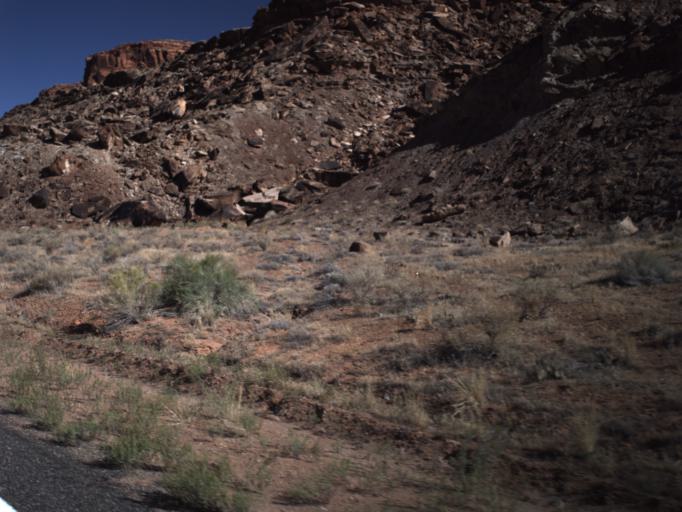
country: US
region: Utah
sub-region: San Juan County
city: Blanding
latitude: 37.9105
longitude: -110.4582
